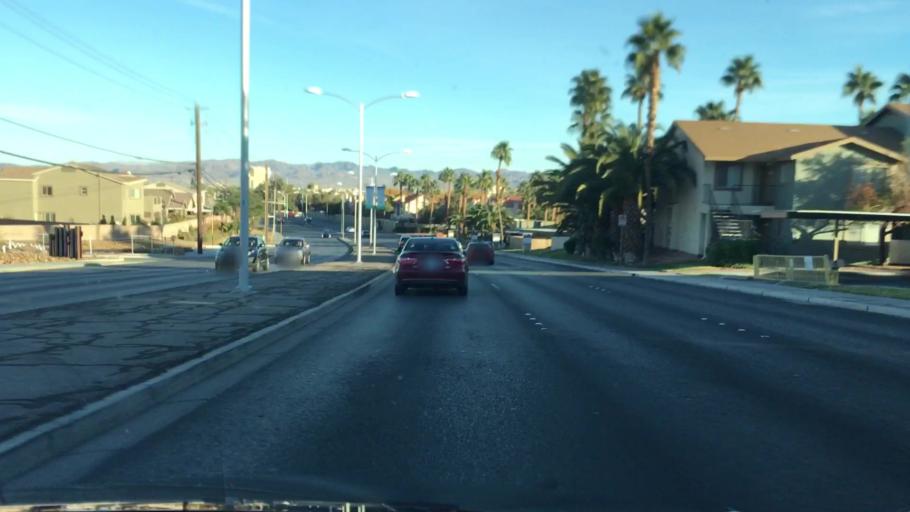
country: US
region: Nevada
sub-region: Clark County
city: Whitney
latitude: 36.0643
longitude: -115.0630
